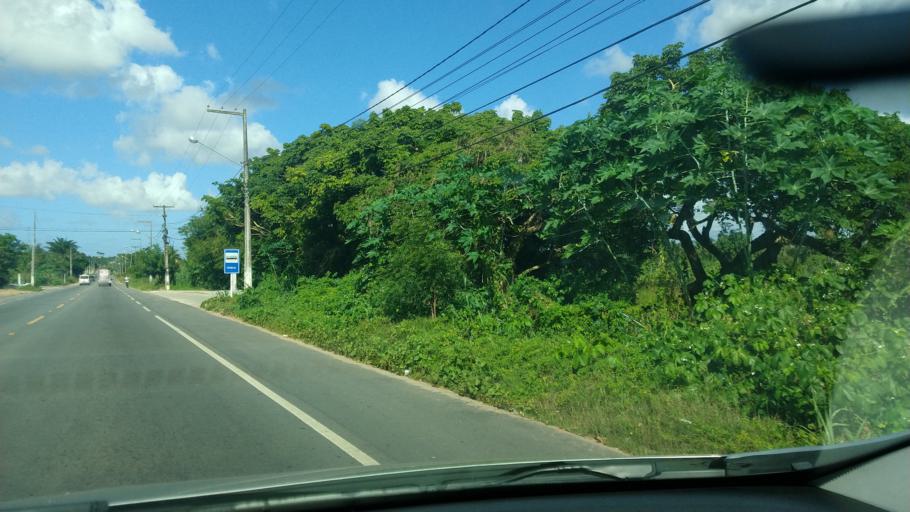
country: BR
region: Rio Grande do Norte
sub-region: Sao Goncalo Do Amarante
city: Sao Goncalo do Amarante
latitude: -5.7880
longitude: -35.3253
